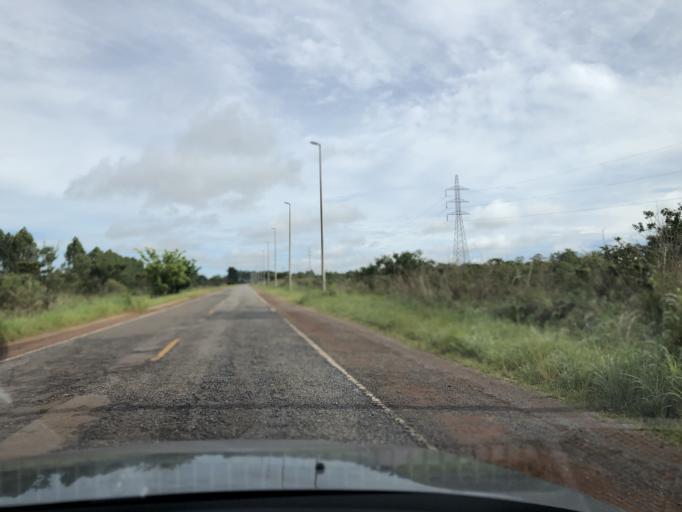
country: BR
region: Federal District
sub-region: Brasilia
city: Brasilia
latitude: -15.6866
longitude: -48.0892
